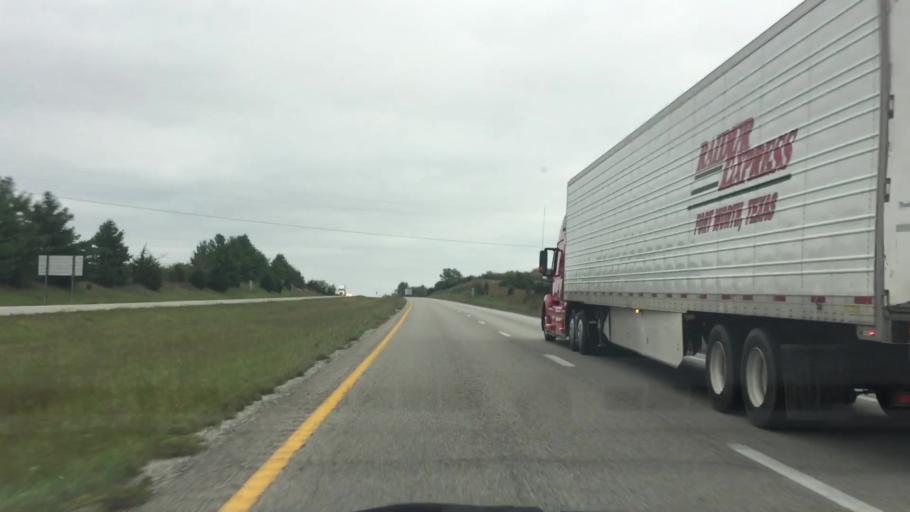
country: US
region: Missouri
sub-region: Clinton County
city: Cameron
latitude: 39.8883
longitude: -94.1576
